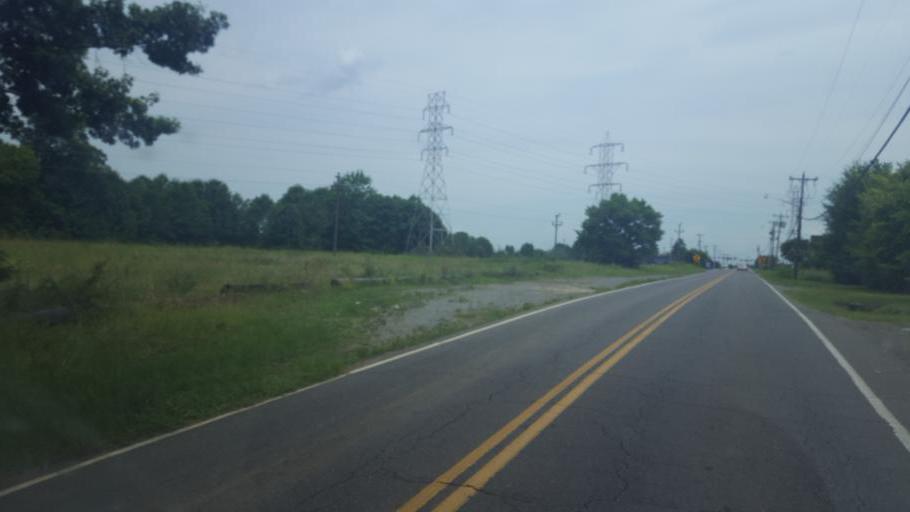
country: US
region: South Carolina
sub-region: York County
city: India Hook
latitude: 34.9746
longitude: -80.9909
